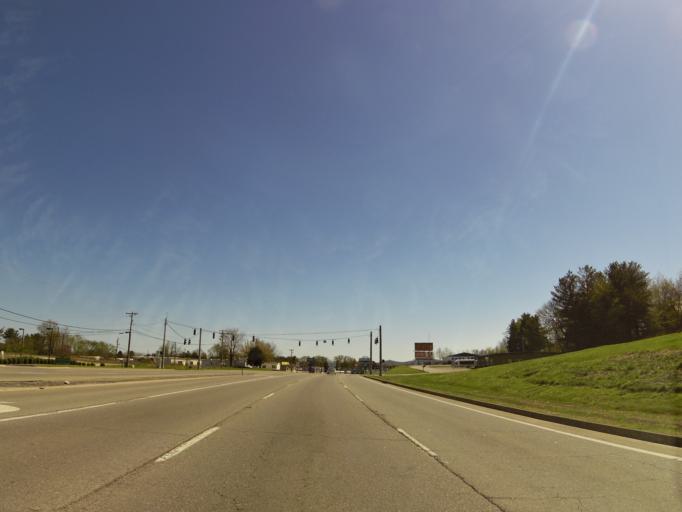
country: US
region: Kentucky
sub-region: Pulaski County
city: Somerset
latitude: 37.0278
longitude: -84.6266
